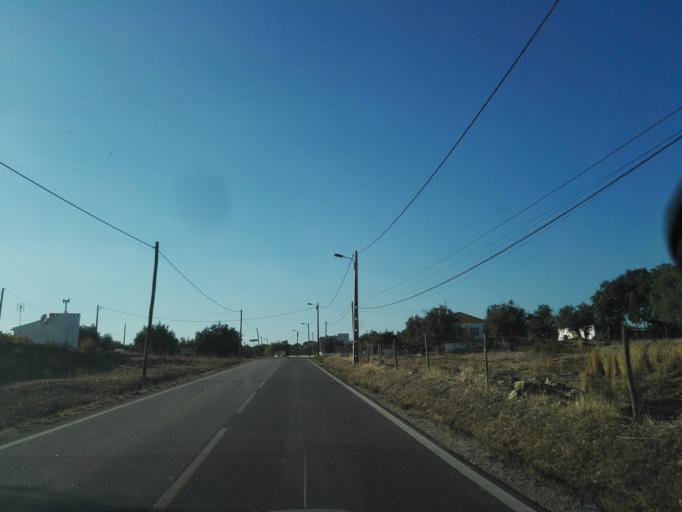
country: PT
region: Portalegre
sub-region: Elvas
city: Elvas
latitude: 38.8801
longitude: -7.1939
